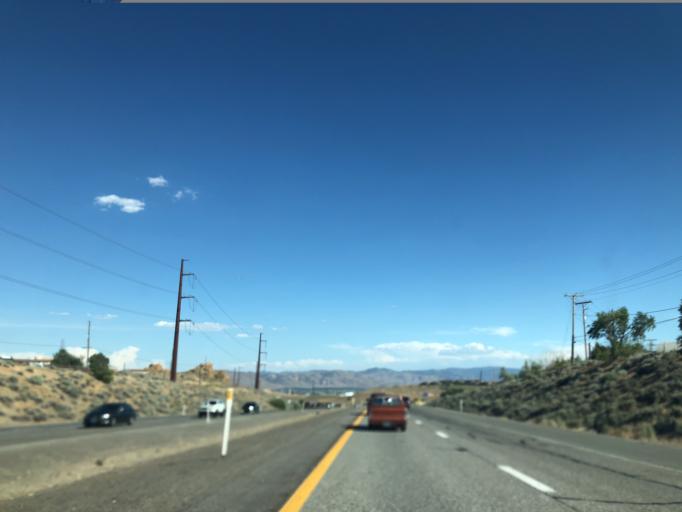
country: US
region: Nevada
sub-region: Washoe County
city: Golden Valley
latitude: 39.5837
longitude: -119.8211
